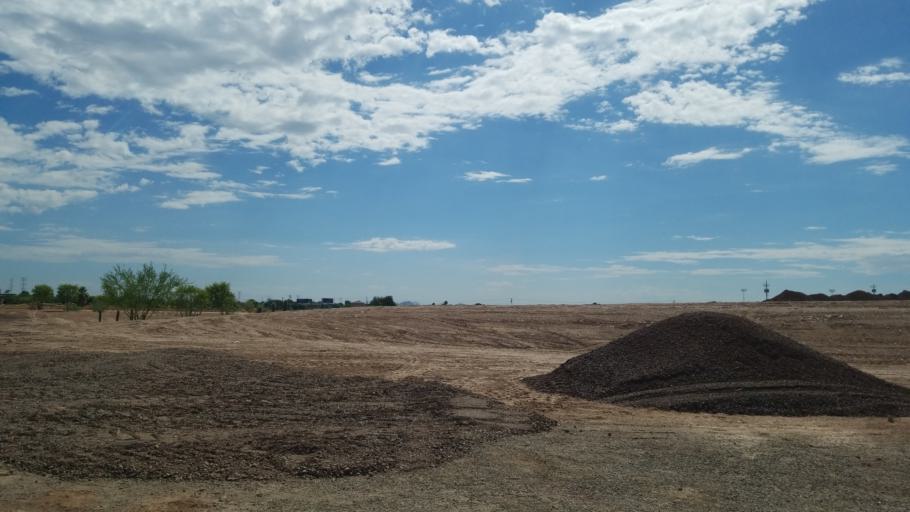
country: US
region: Arizona
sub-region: Maricopa County
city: Peoria
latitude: 33.5494
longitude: -112.2599
